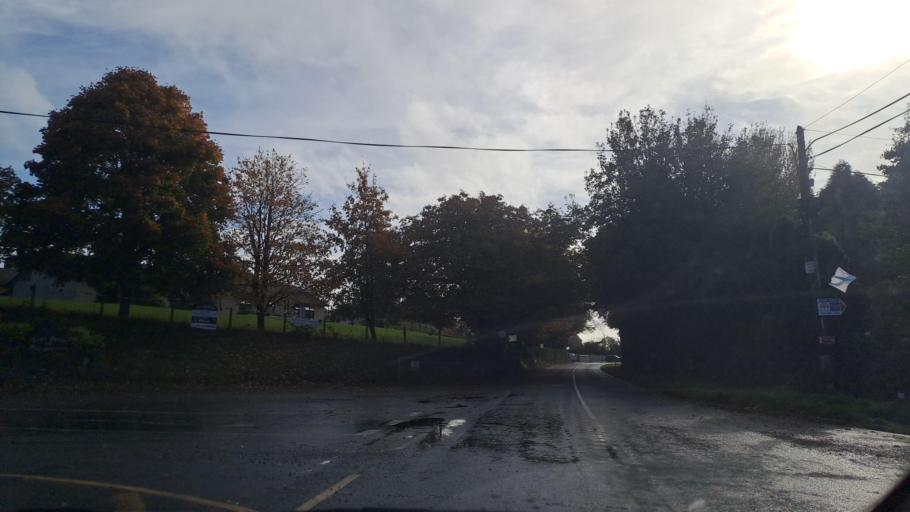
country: IE
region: Ulster
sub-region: County Monaghan
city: Carrickmacross
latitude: 53.9221
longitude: -6.7126
